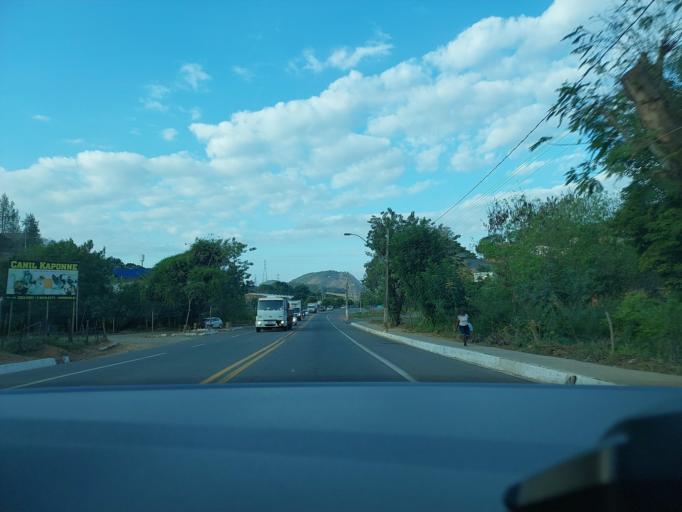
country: BR
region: Minas Gerais
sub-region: Muriae
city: Muriae
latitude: -21.1277
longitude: -42.3452
